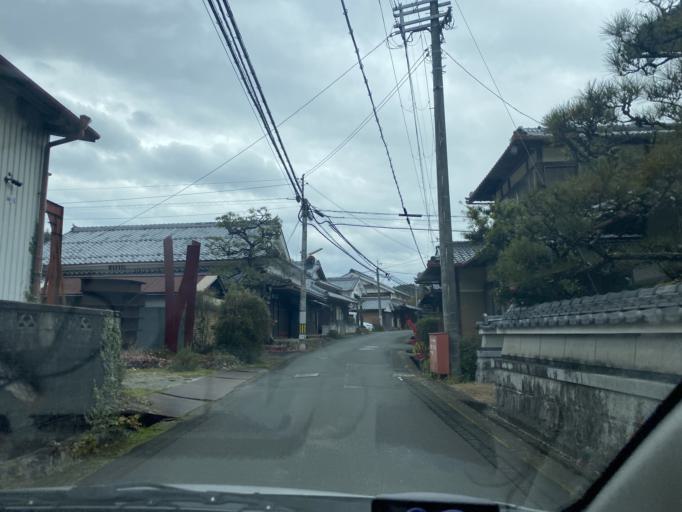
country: JP
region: Kyoto
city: Kameoka
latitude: 35.0577
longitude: 135.4474
